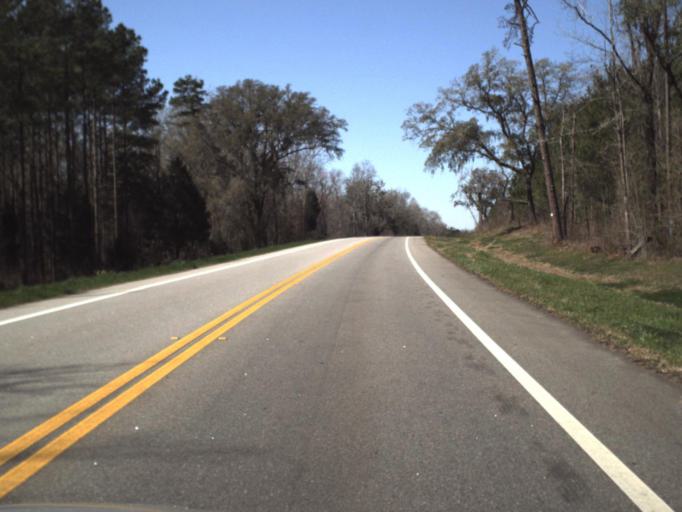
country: US
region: Florida
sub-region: Jackson County
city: Marianna
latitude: 30.8221
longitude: -85.3250
